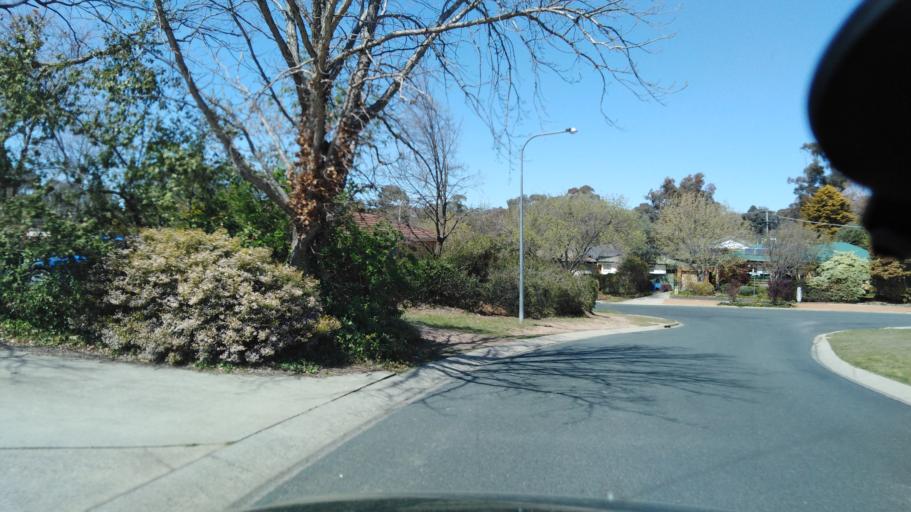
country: AU
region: Australian Capital Territory
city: Forrest
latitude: -35.3464
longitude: 149.0343
